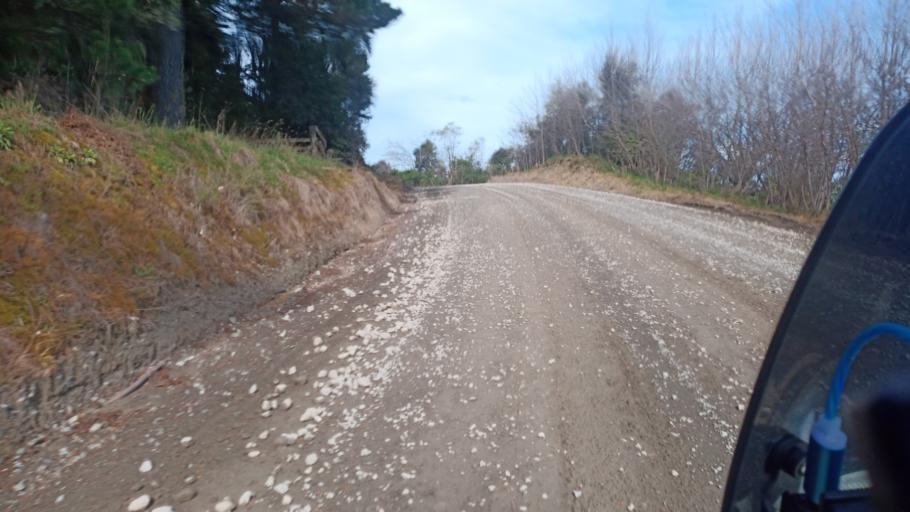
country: NZ
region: Gisborne
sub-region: Gisborne District
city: Gisborne
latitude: -38.1298
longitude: 178.1799
